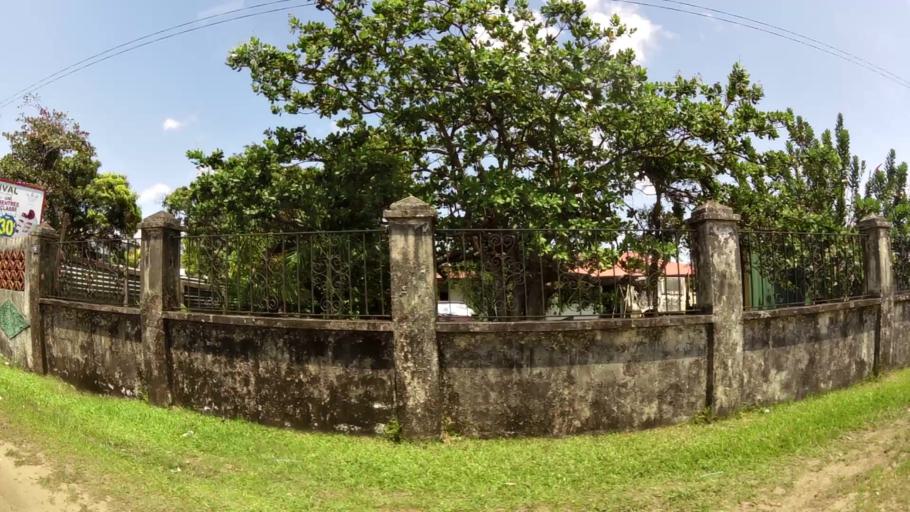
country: GF
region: Guyane
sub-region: Guyane
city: Cayenne
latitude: 4.9032
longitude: -52.3260
